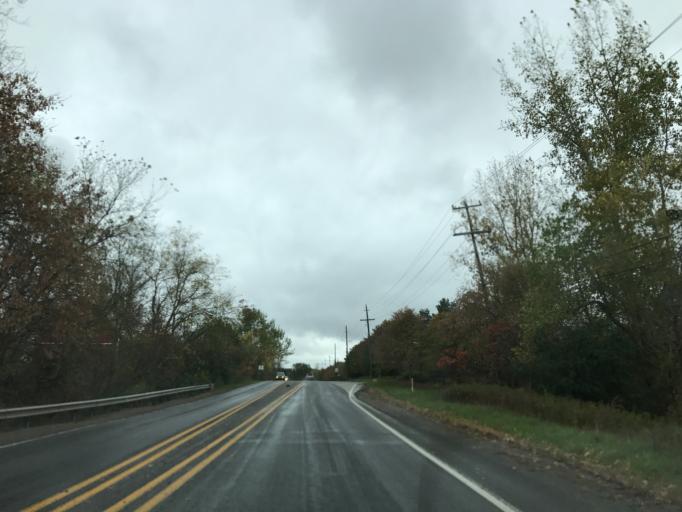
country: US
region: Michigan
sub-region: Washtenaw County
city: Ypsilanti
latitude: 42.3077
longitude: -83.6624
